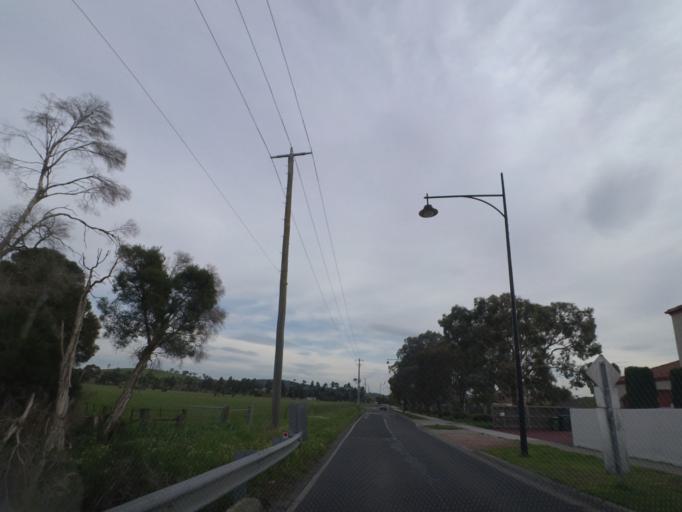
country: AU
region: Victoria
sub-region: Knox
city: Ferntree Gully
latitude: -37.8972
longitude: 145.2822
